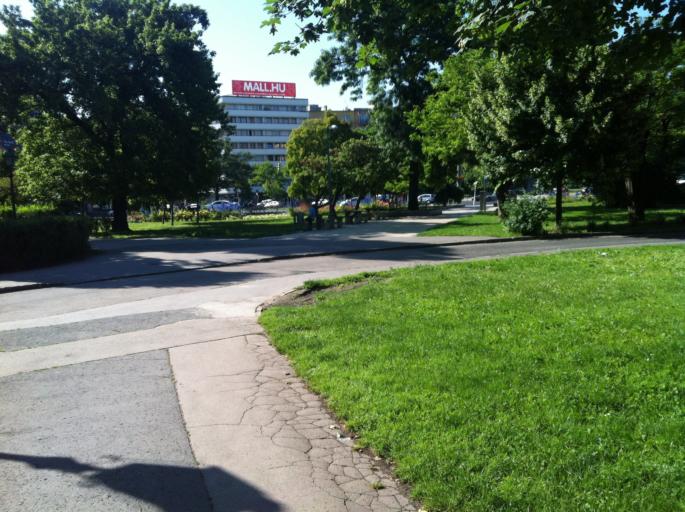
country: HU
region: Budapest
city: Budapest XI. keruelet
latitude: 47.4762
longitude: 19.0406
